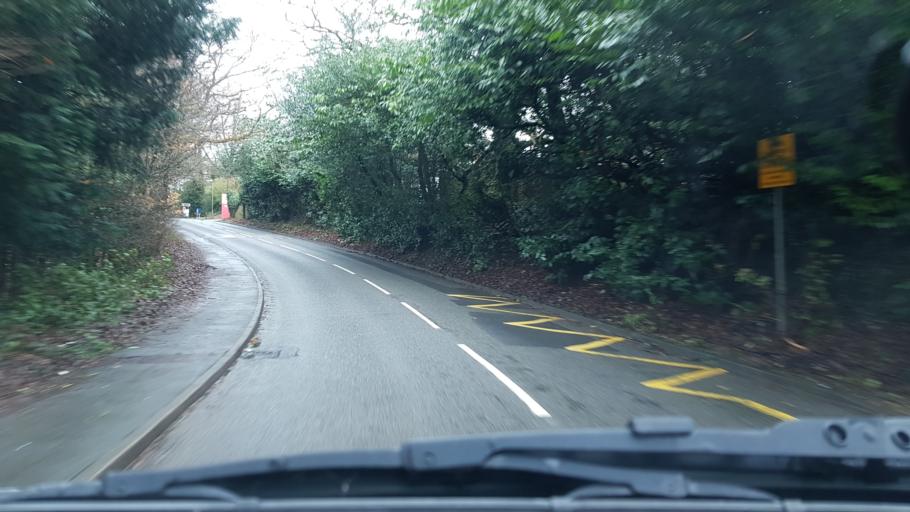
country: GB
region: England
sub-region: Surrey
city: Hindhead
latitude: 51.0927
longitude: -0.7495
